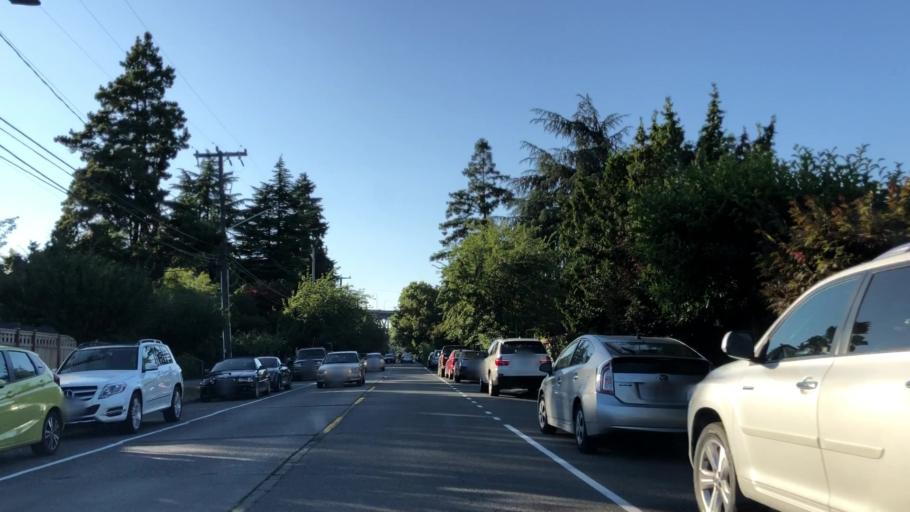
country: US
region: Washington
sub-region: King County
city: Seattle
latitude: 47.6480
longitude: -122.3181
